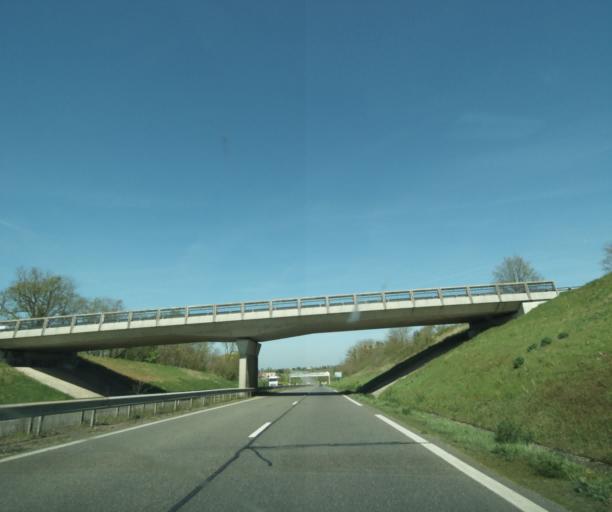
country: FR
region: Bourgogne
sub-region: Departement de la Nievre
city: Saint-Pierre-le-Moutier
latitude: 46.7846
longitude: 3.1274
